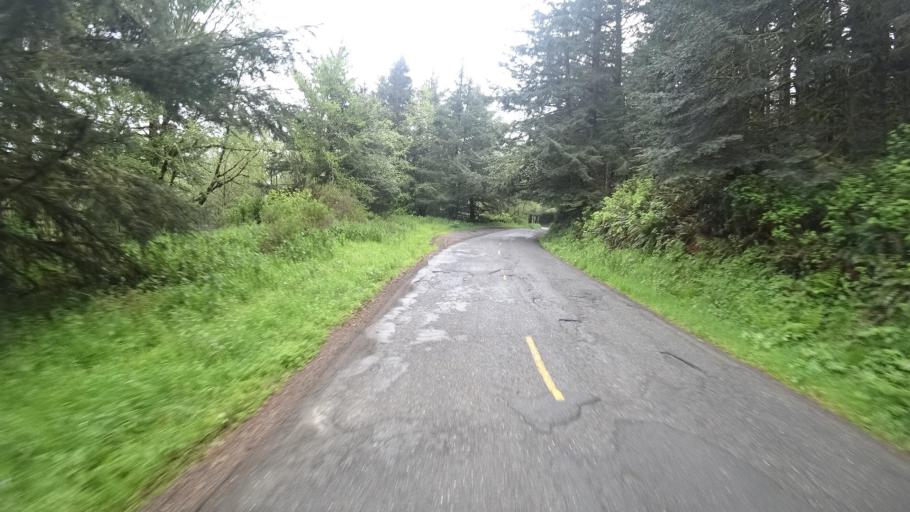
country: US
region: California
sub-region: Humboldt County
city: Ferndale
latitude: 40.5063
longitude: -124.2911
